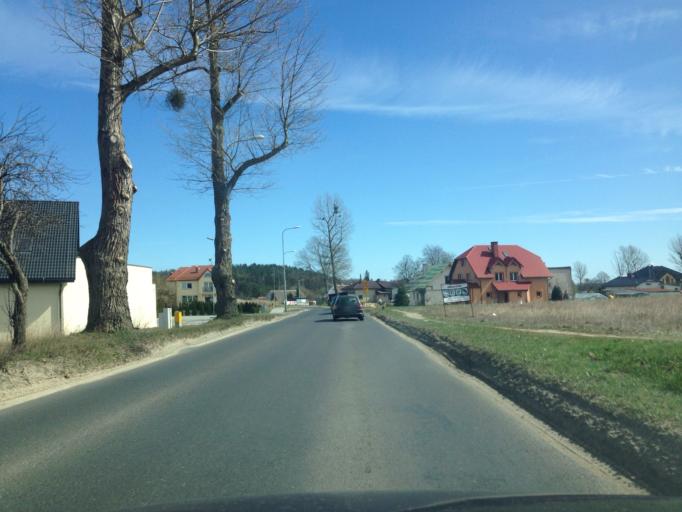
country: PL
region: Pomeranian Voivodeship
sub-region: Powiat kartuski
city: Chwaszczyno
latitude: 54.4850
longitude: 18.4350
